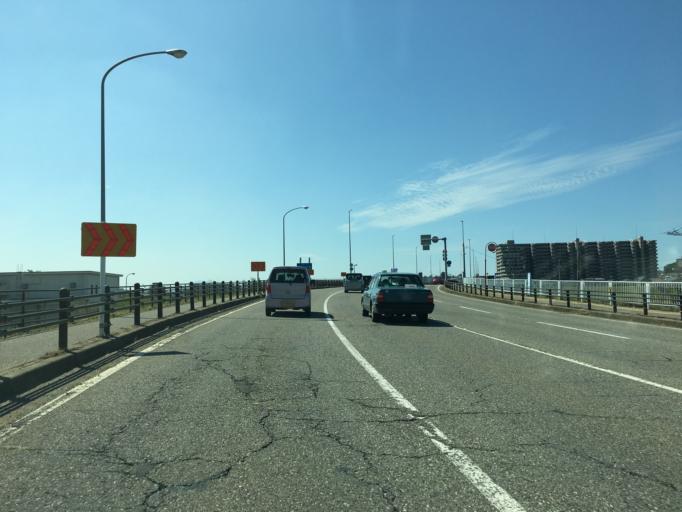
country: JP
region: Niigata
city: Niigata-shi
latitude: 37.8986
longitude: 139.0124
